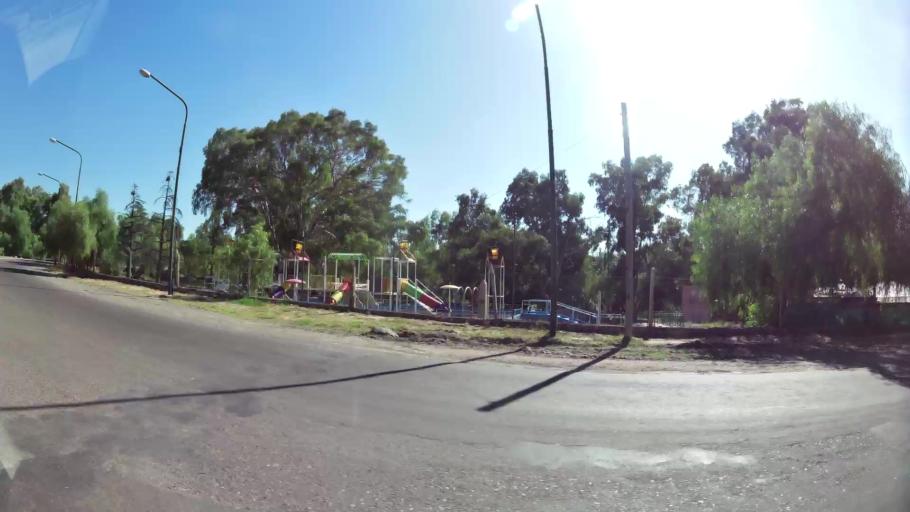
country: AR
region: Mendoza
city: Mendoza
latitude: -32.8907
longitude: -68.8848
